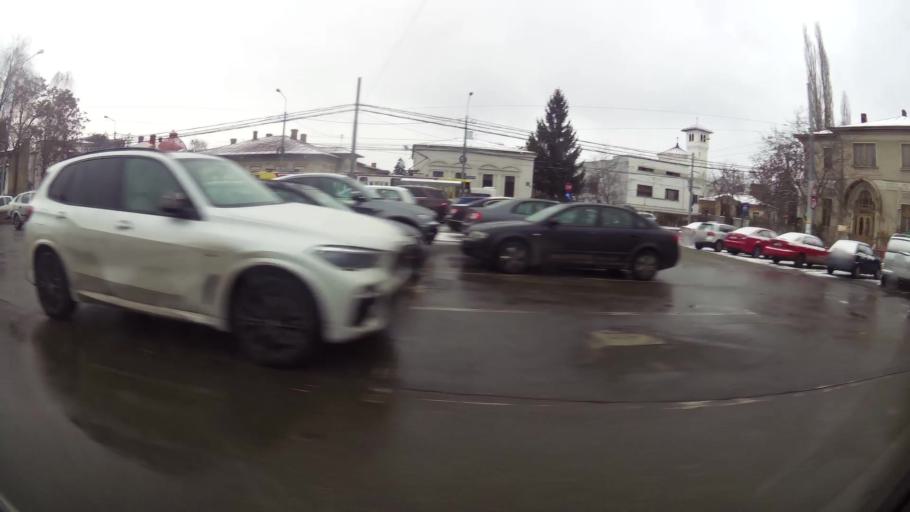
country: RO
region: Prahova
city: Ploiesti
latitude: 44.9381
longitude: 26.0278
